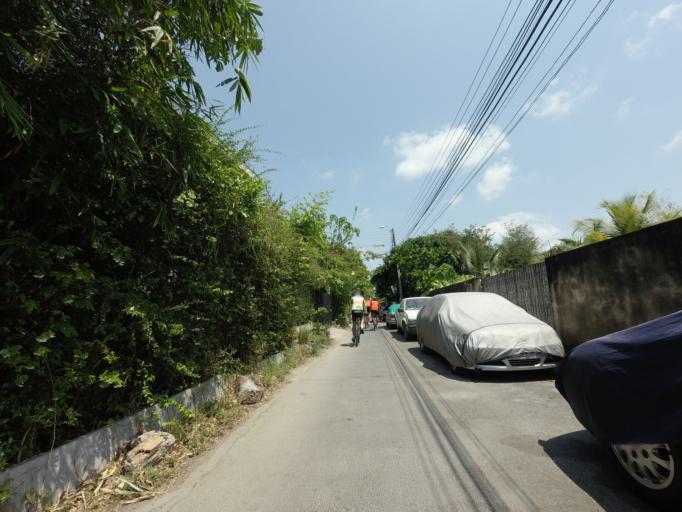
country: TH
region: Bangkok
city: Chom Thong
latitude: 13.6548
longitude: 100.4751
